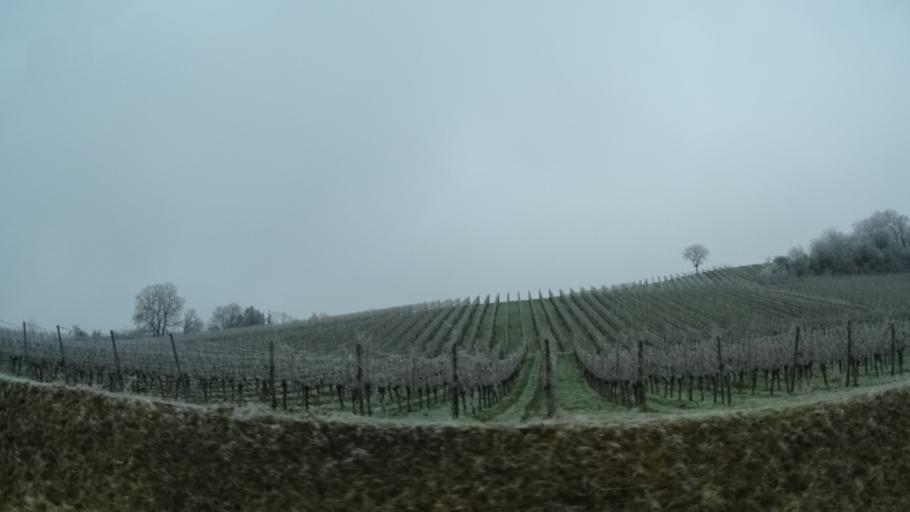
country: DE
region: Bavaria
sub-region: Regierungsbezirk Unterfranken
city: Segnitz
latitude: 49.6821
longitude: 10.1407
